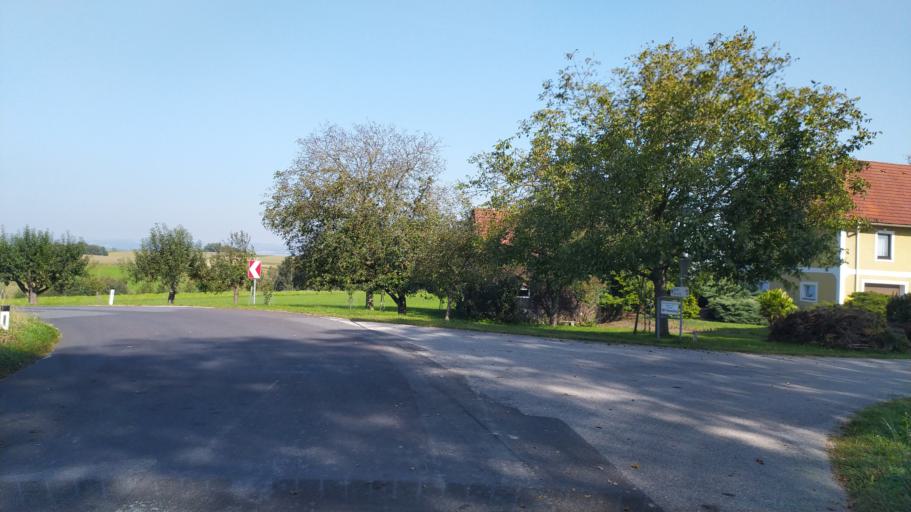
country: AT
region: Lower Austria
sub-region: Politischer Bezirk Amstetten
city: Zeillern
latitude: 48.1430
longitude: 14.7539
